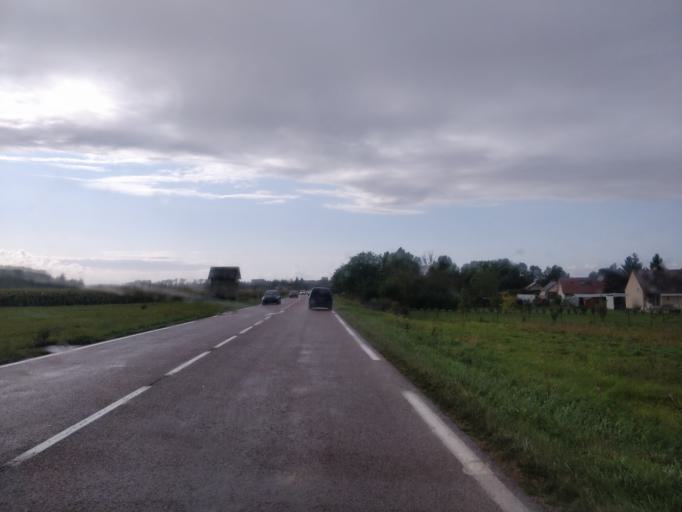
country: FR
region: Champagne-Ardenne
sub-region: Departement de l'Aube
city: Lusigny-sur-Barse
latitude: 48.2445
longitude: 4.2801
